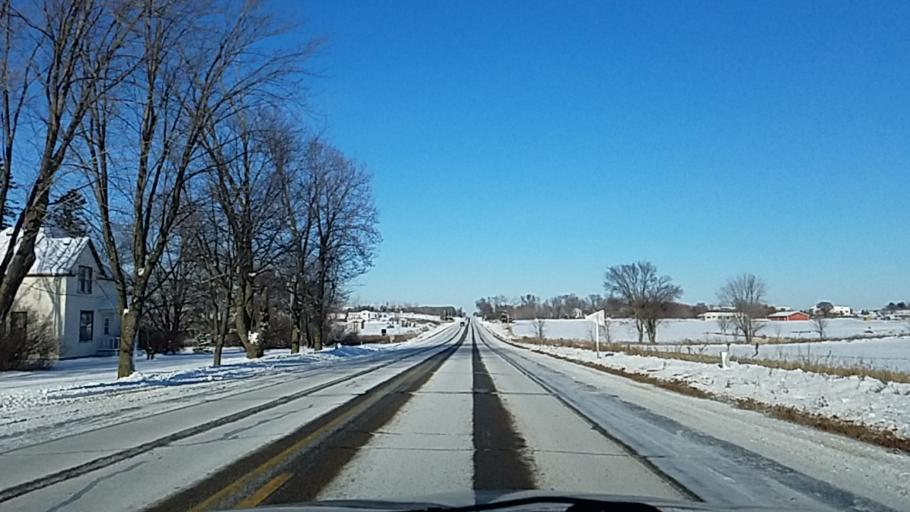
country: US
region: Wisconsin
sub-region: Saint Croix County
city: New Richmond
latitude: 45.0670
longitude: -92.5375
